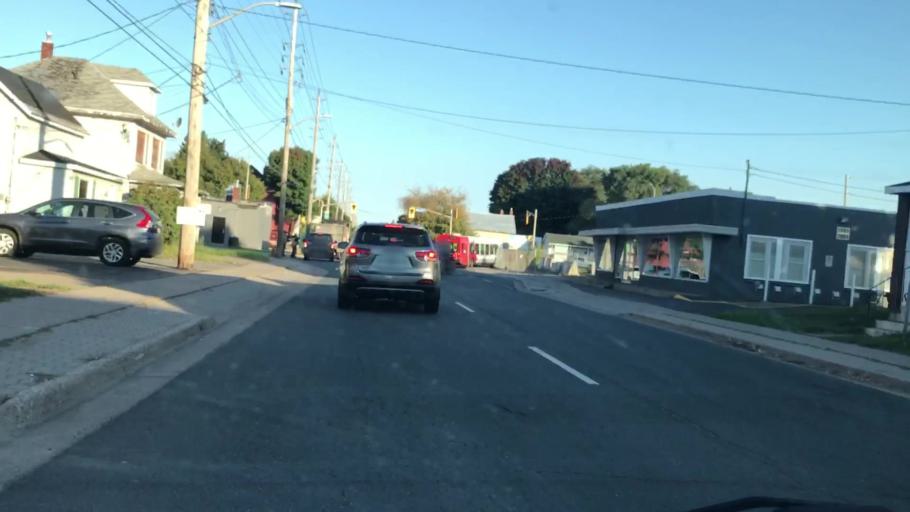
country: CA
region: Ontario
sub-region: Algoma
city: Sault Ste. Marie
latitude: 46.5148
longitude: -84.3323
